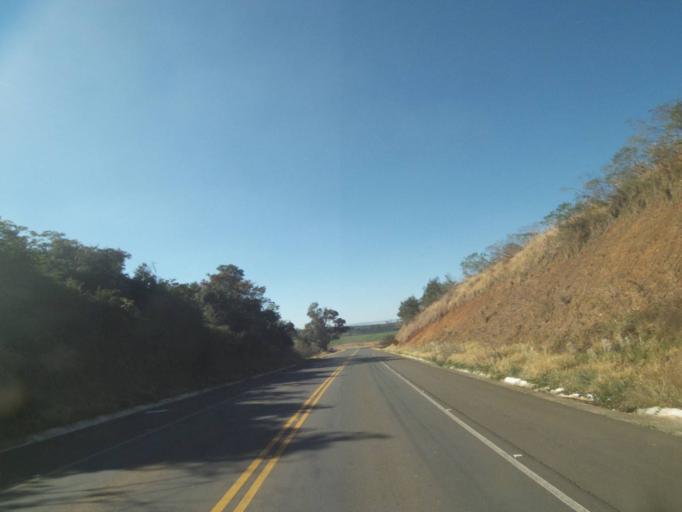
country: BR
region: Parana
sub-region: Tibagi
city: Tibagi
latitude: -24.7489
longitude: -50.4640
